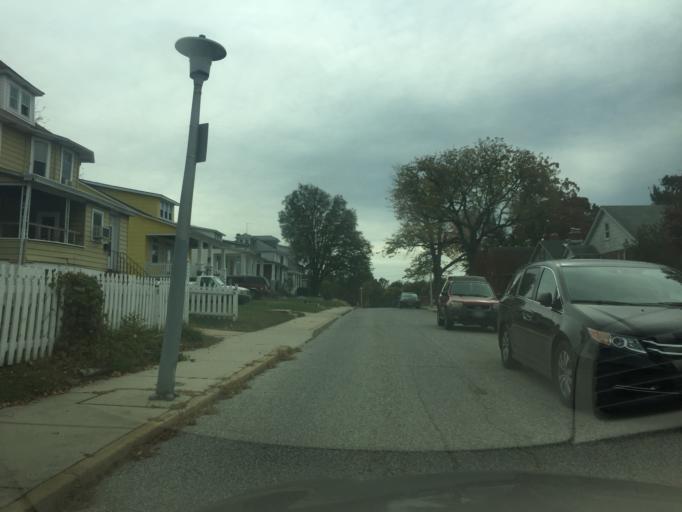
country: US
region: Maryland
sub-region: Baltimore County
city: Parkville
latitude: 39.3557
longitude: -76.5617
